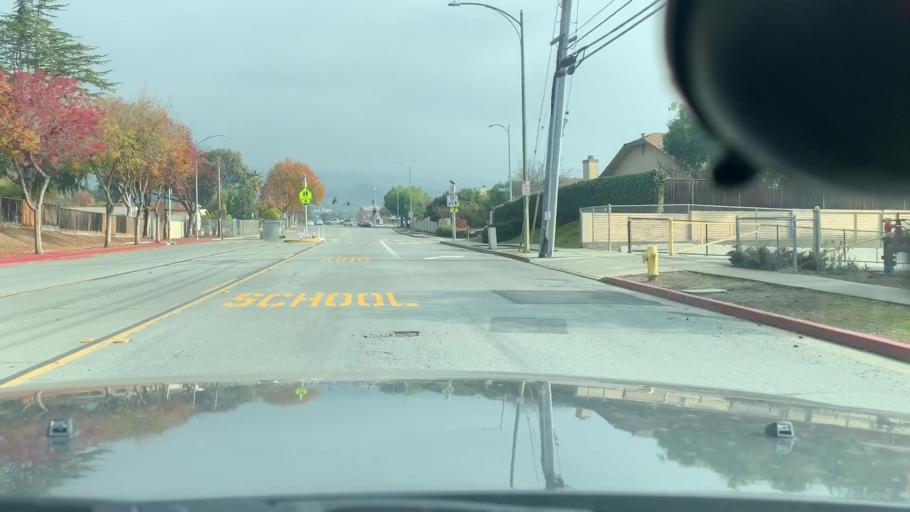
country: US
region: California
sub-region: Santa Clara County
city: Alum Rock
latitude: 37.3248
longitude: -121.7846
